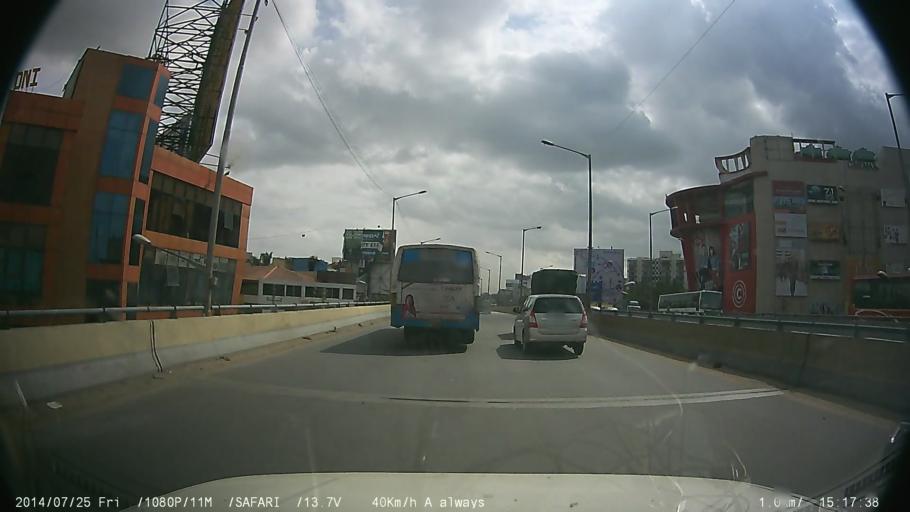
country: IN
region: Karnataka
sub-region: Bangalore Urban
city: Bangalore
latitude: 12.9258
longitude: 77.6764
